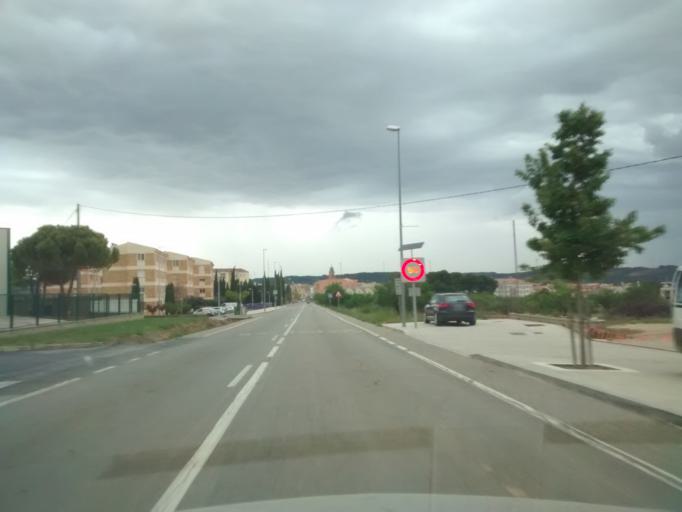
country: ES
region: Catalonia
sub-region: Provincia de Tarragona
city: Gandesa
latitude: 41.0491
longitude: 0.4457
